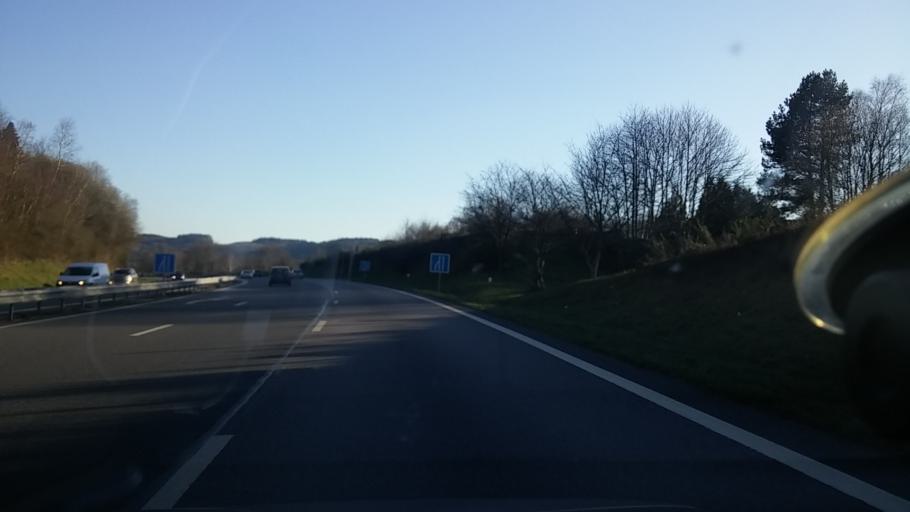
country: FR
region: Limousin
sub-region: Departement de la Haute-Vienne
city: Bessines-sur-Gartempe
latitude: 46.0836
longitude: 1.3568
